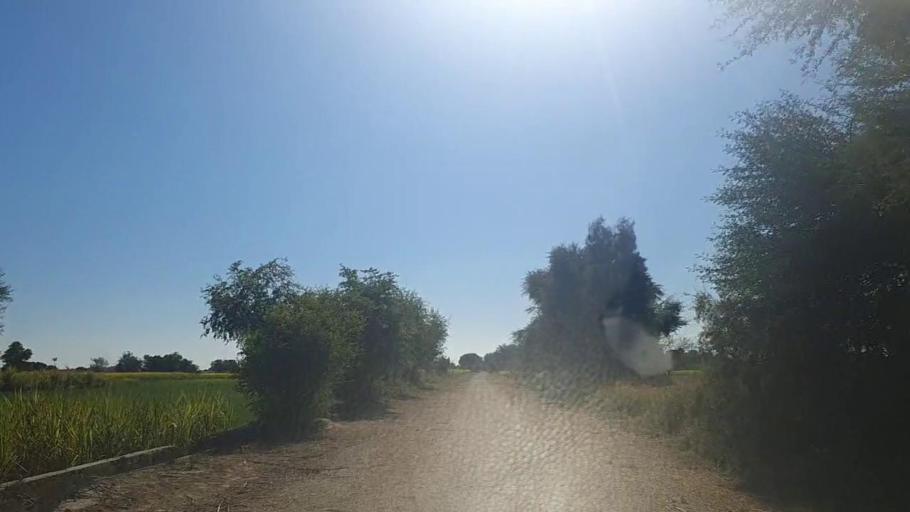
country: PK
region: Sindh
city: Sanghar
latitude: 26.1974
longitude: 68.9105
